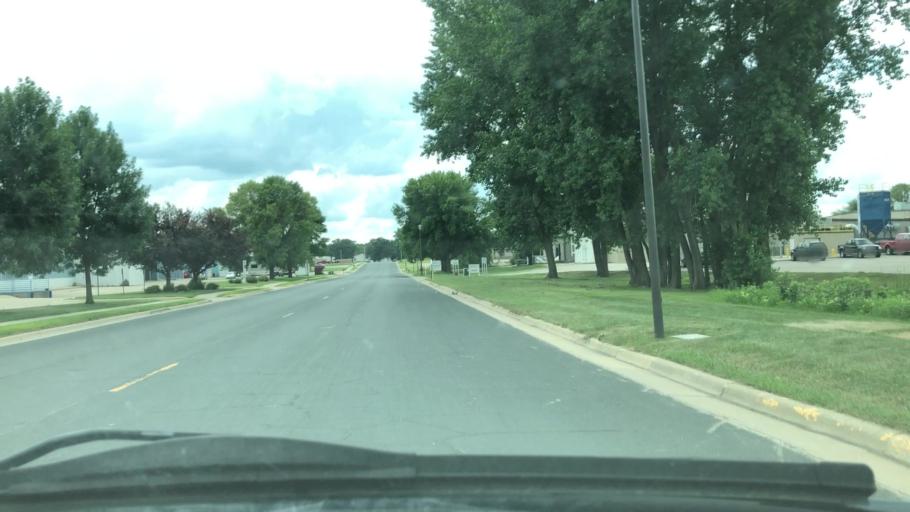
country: US
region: Minnesota
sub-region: Olmsted County
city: Stewartville
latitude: 43.8674
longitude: -92.4900
